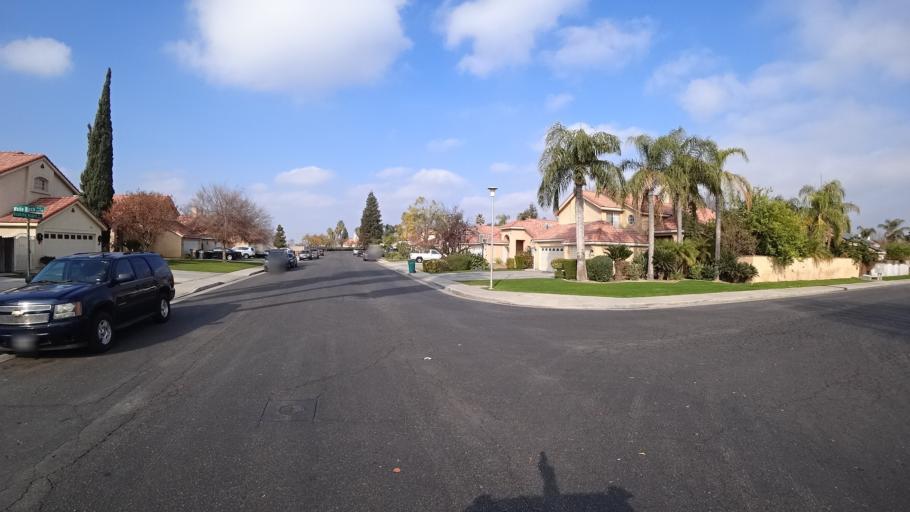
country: US
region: California
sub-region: Kern County
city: Greenacres
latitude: 35.2984
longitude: -119.0896
